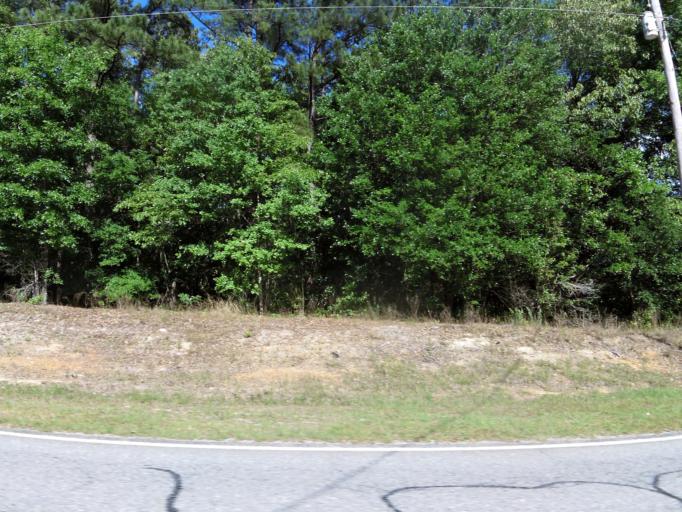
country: US
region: South Carolina
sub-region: Bamberg County
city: Denmark
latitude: 33.2173
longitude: -81.1750
